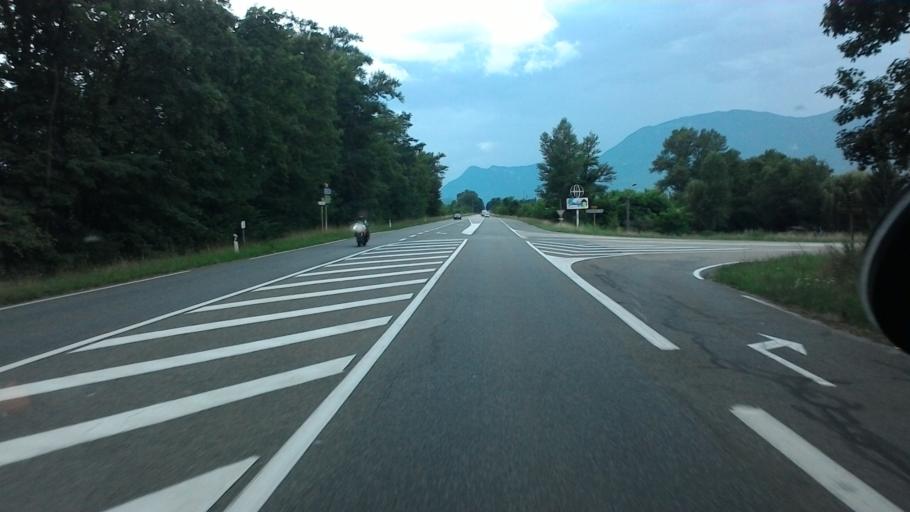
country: FR
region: Rhone-Alpes
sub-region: Departement de la Savoie
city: Aiton
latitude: 45.5706
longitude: 6.2257
